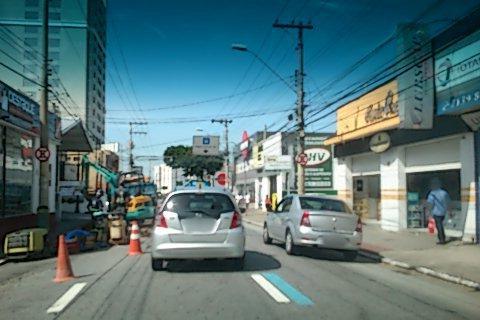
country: BR
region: Sao Paulo
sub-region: Sao Jose Dos Campos
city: Sao Jose dos Campos
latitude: -23.1980
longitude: -45.8871
